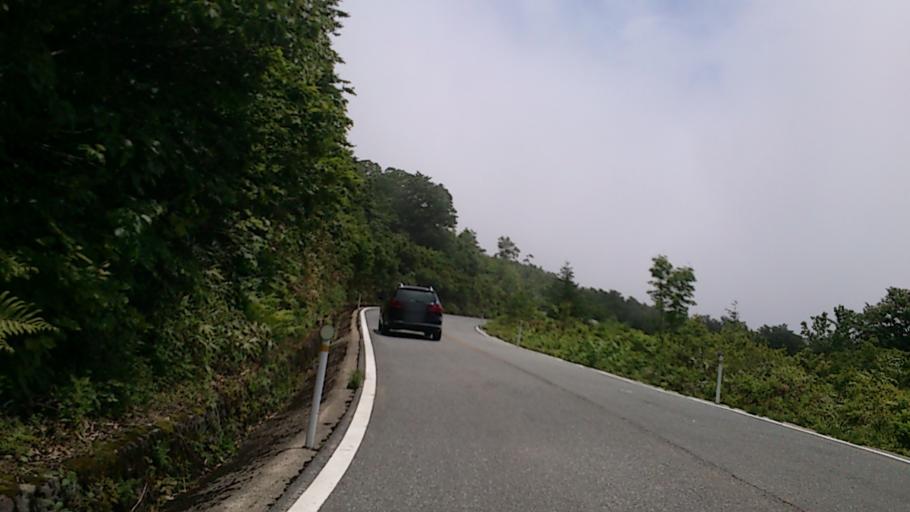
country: JP
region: Yamagata
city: Yamagata-shi
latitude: 38.1176
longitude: 140.4219
